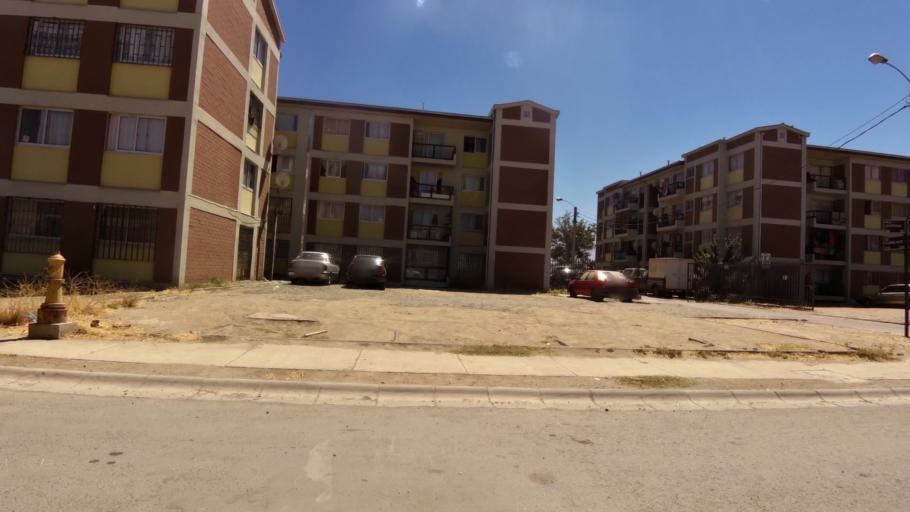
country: CL
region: O'Higgins
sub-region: Provincia de Cachapoal
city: Rancagua
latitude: -34.1558
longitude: -70.7202
